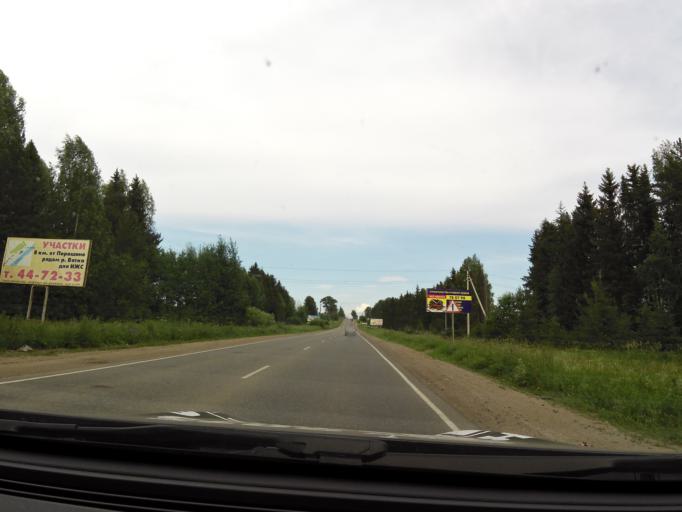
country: RU
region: Kirov
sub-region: Kirovo-Chepetskiy Rayon
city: Kirov
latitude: 58.6265
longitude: 49.8013
